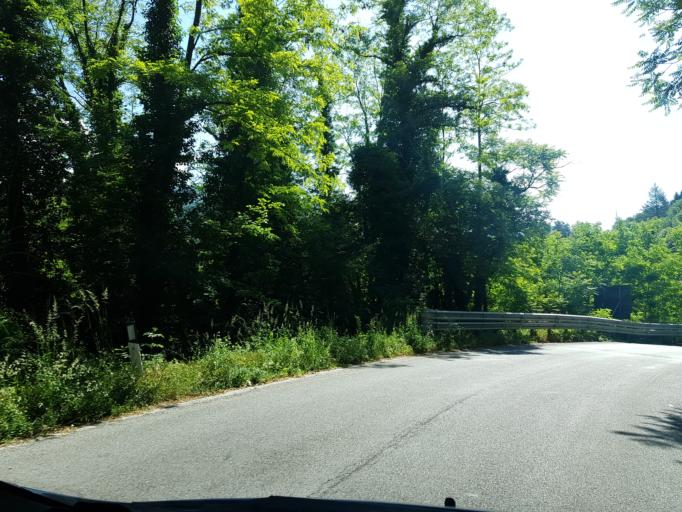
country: IT
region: Tuscany
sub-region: Provincia di Lucca
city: Camporgiano
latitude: 44.1697
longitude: 10.3185
